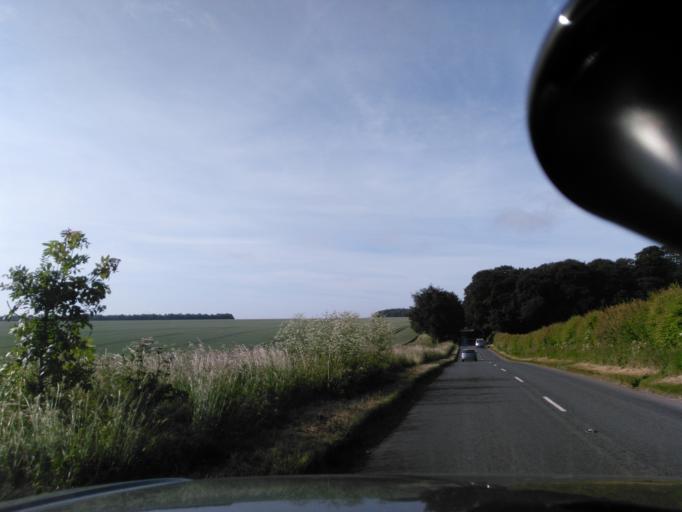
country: GB
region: England
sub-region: Wiltshire
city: Winterbourne Stoke
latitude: 51.1639
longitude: -1.8591
